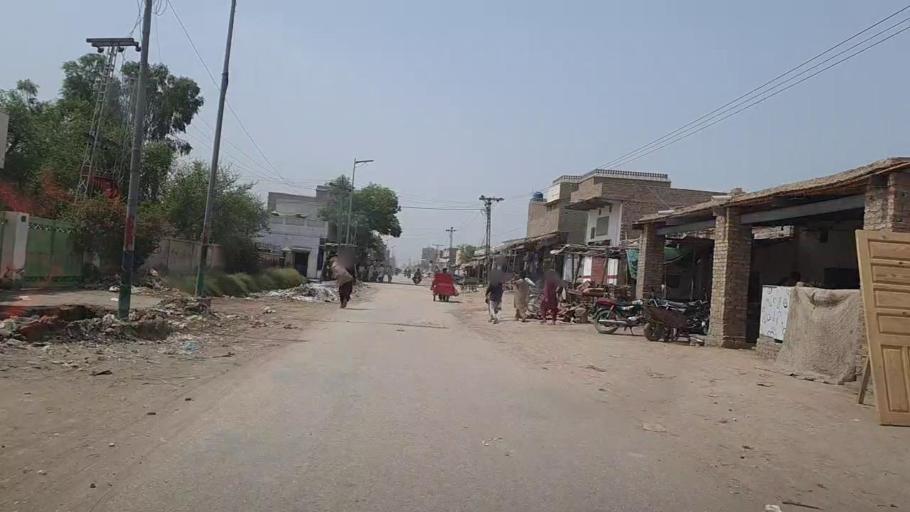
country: PK
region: Sindh
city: Radhan
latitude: 27.1751
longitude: 67.9485
